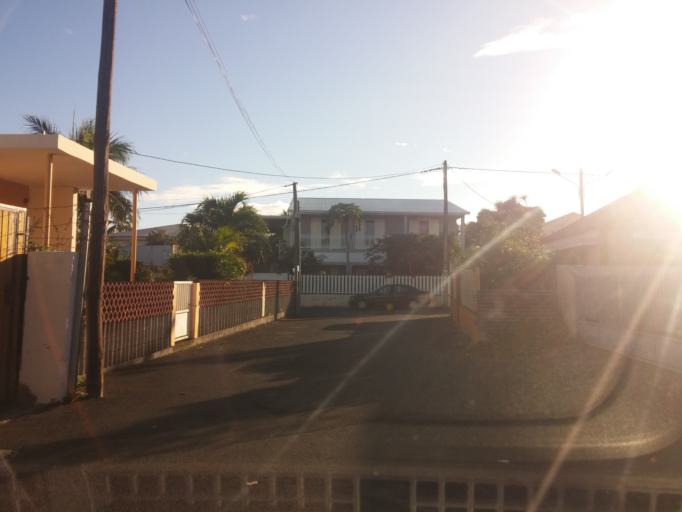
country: RE
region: Reunion
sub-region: Reunion
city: Le Port
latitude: -20.9349
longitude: 55.2944
